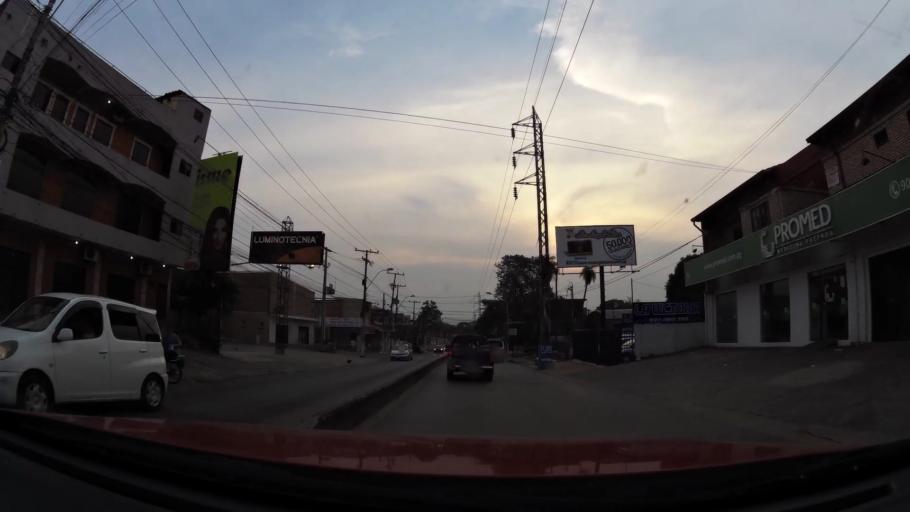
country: PY
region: Central
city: Lambare
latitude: -25.3421
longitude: -57.6049
